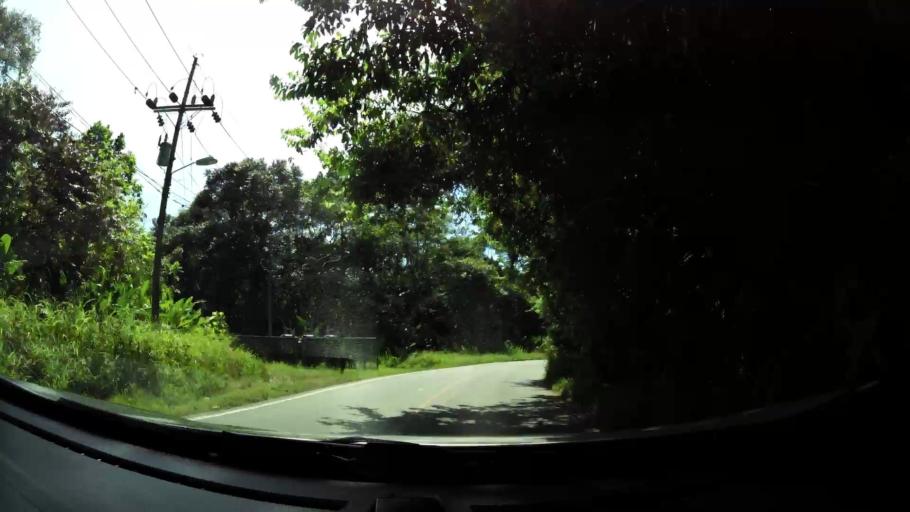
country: CR
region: San Jose
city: San Isidro
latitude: 9.2622
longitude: -83.8629
